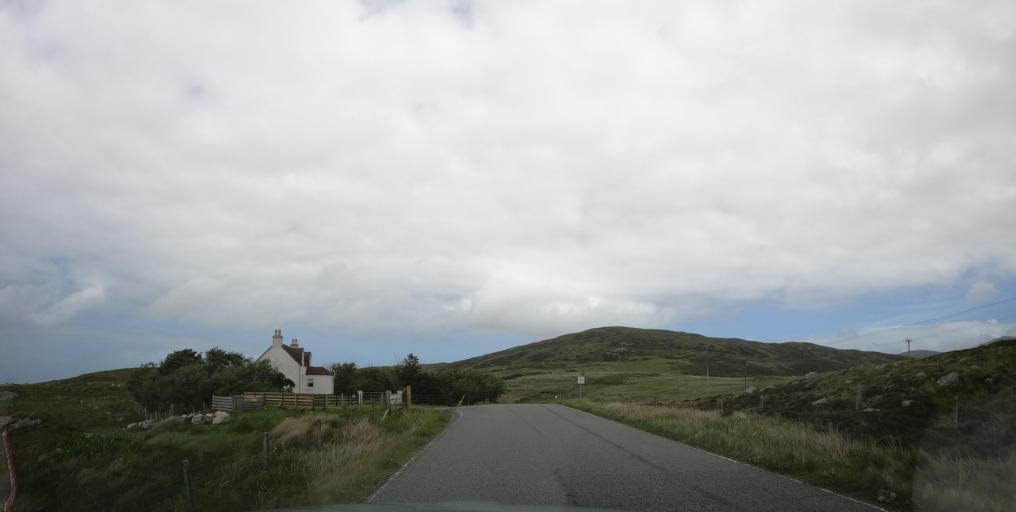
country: GB
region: Scotland
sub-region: Eilean Siar
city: Isle of South Uist
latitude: 57.2931
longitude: -7.3651
